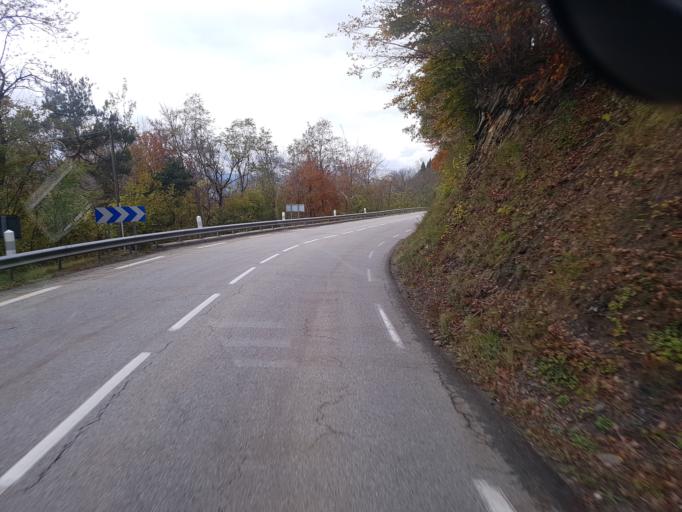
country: FR
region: Rhone-Alpes
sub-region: Departement de l'Isere
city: La Motte-Saint-Martin
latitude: 44.9379
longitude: 5.6406
